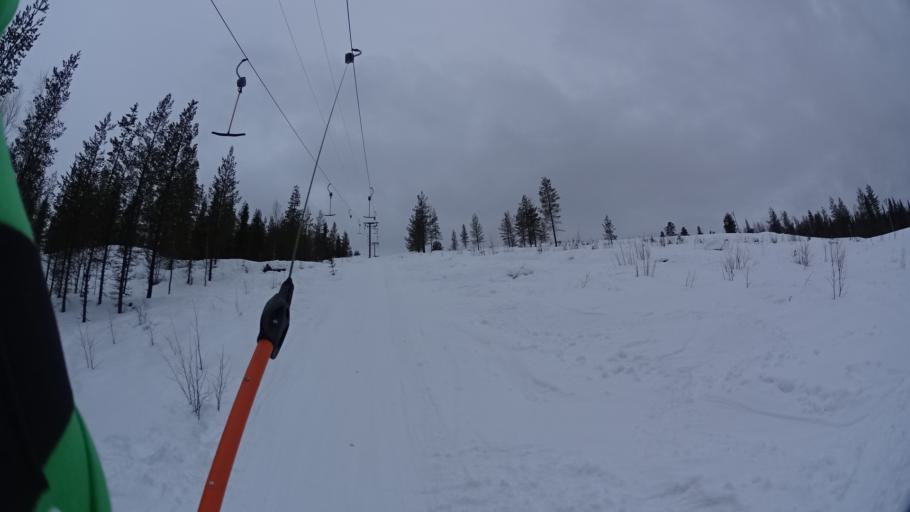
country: SE
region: Vaesterbotten
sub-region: Mala Kommun
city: Mala
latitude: 65.1801
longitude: 18.7691
